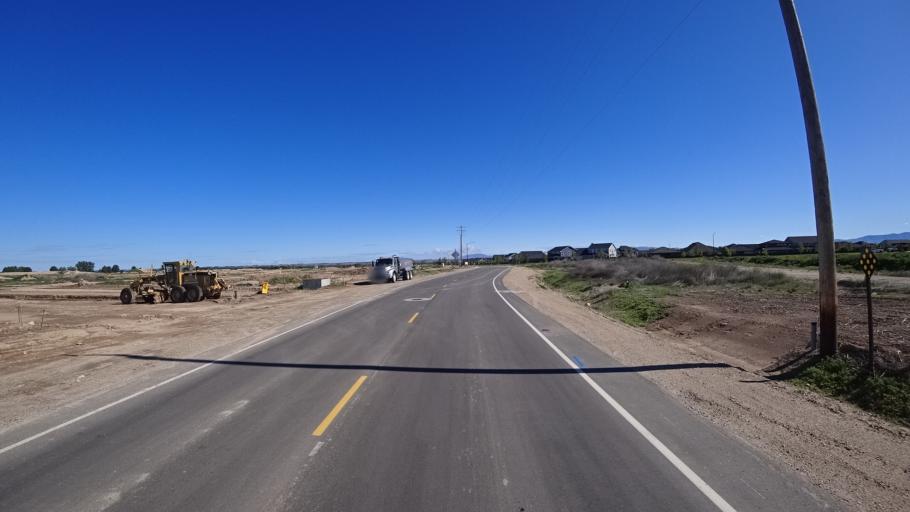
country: US
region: Idaho
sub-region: Ada County
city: Star
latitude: 43.6646
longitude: -116.4536
